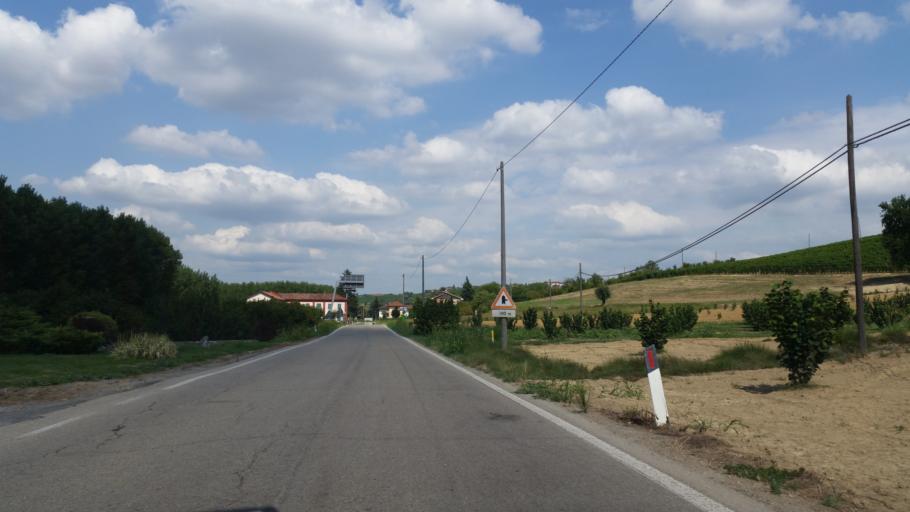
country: IT
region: Piedmont
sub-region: Provincia di Cuneo
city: Neive-Borgonovo
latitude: 44.7098
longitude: 8.1089
